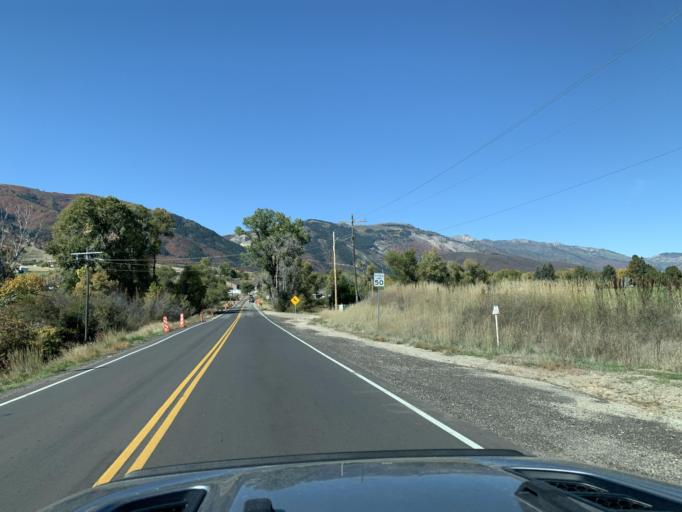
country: US
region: Utah
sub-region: Weber County
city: Wolf Creek
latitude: 41.3133
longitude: -111.8391
